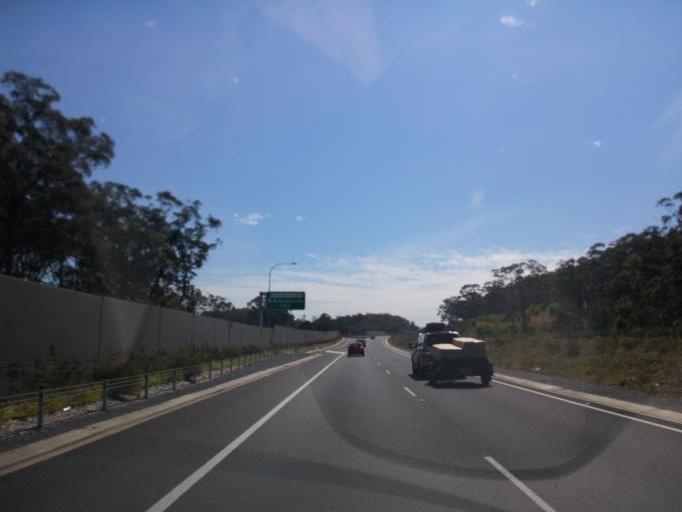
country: AU
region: New South Wales
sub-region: Great Lakes
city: Bulahdelah
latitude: -32.4054
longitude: 152.2157
